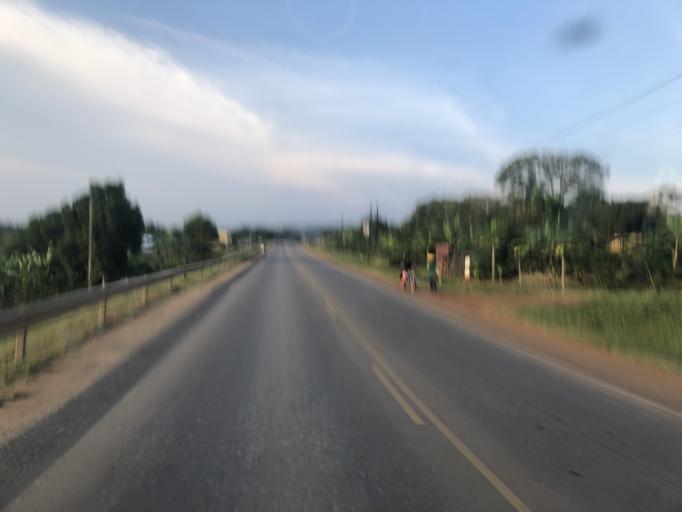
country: UG
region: Central Region
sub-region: Mpigi District
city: Mpigi
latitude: 0.1987
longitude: 32.2991
